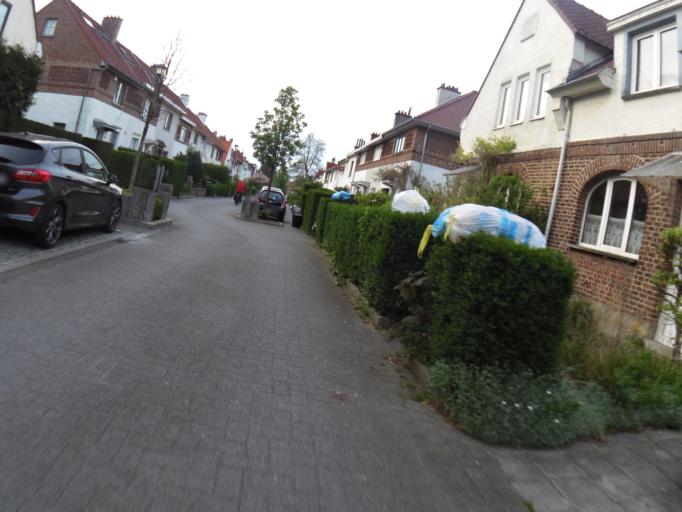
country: BE
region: Flanders
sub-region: Provincie Vlaams-Brabant
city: Wezembeek-Oppem
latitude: 50.8232
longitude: 4.4615
